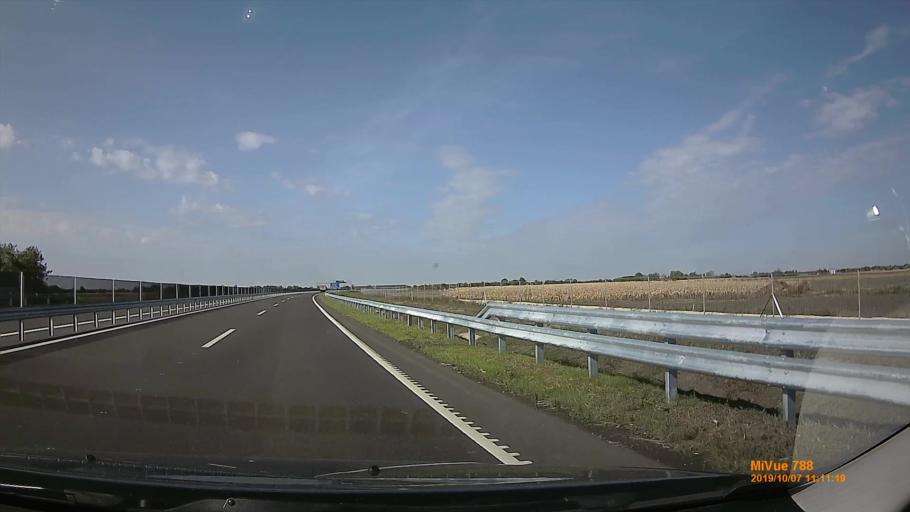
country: HU
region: Bekes
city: Kondoros
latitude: 46.7374
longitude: 20.8011
